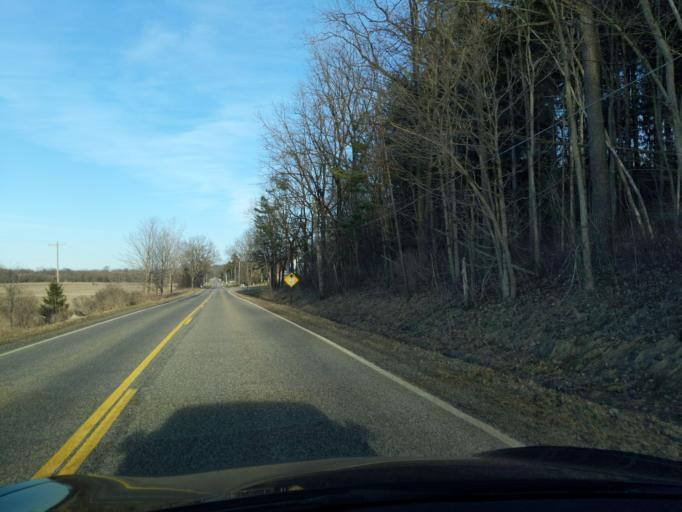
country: US
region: Michigan
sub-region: Ionia County
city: Ionia
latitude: 42.9649
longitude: -85.0851
